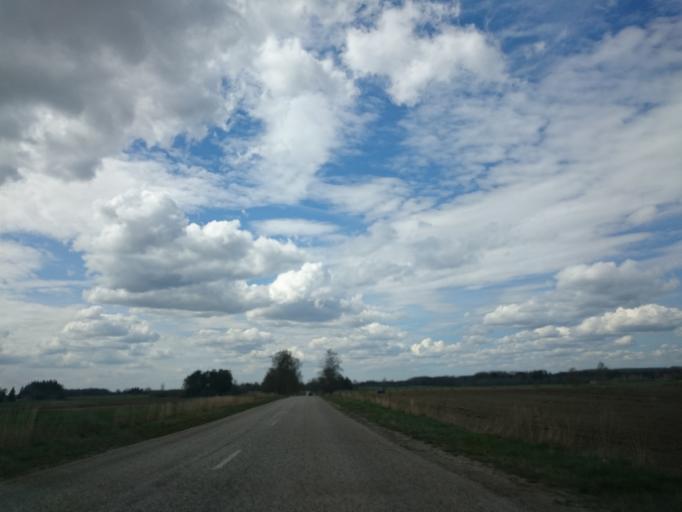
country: LV
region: Talsu Rajons
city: Sabile
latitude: 56.9500
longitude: 22.3486
